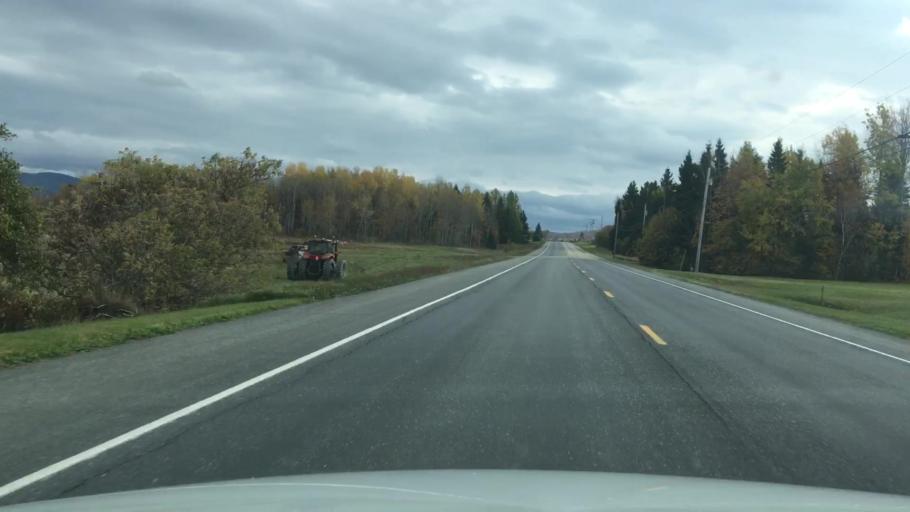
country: US
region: Maine
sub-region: Aroostook County
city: Easton
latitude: 46.5619
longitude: -67.9449
